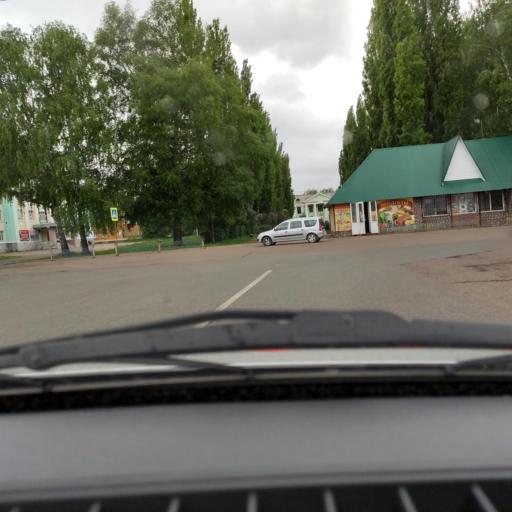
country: RU
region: Bashkortostan
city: Sterlitamak
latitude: 53.6893
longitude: 55.9456
